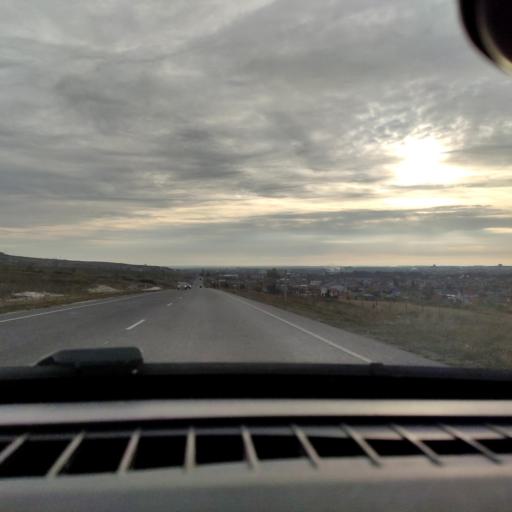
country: RU
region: Belgorod
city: Alekseyevka
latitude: 50.6456
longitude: 38.6372
